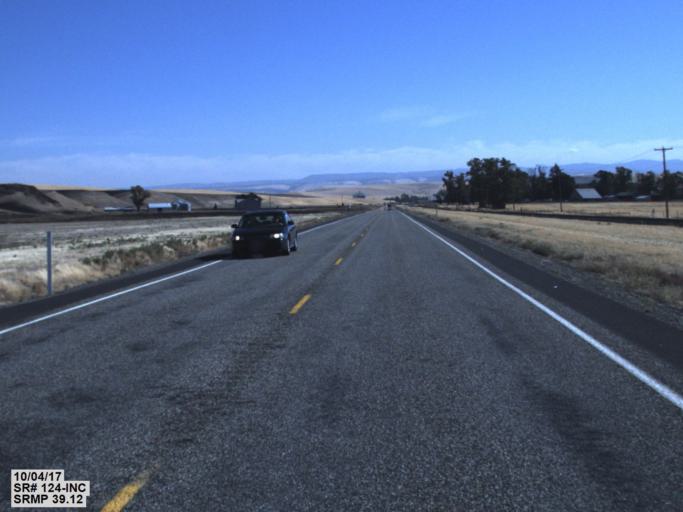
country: US
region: Washington
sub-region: Walla Walla County
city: Waitsburg
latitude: 46.2894
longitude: -118.2556
